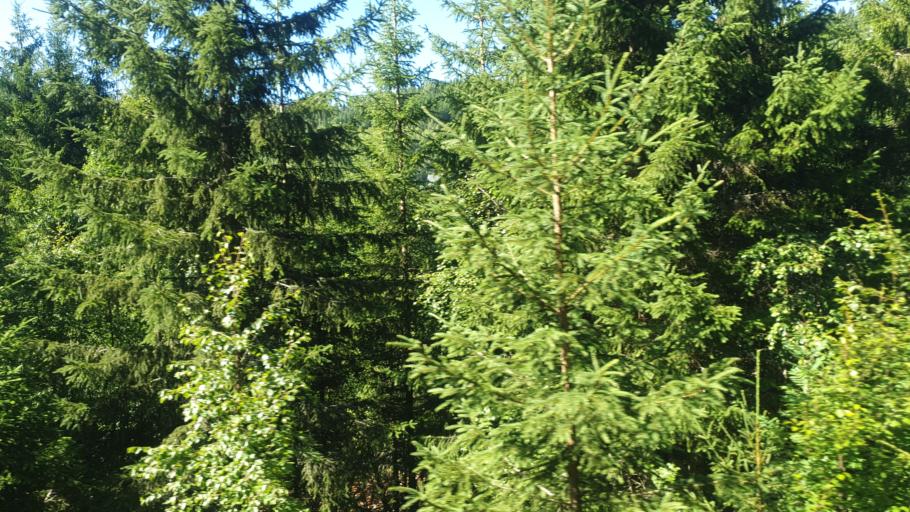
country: NO
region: Sor-Trondelag
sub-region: Meldal
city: Meldal
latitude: 63.1397
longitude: 9.7120
